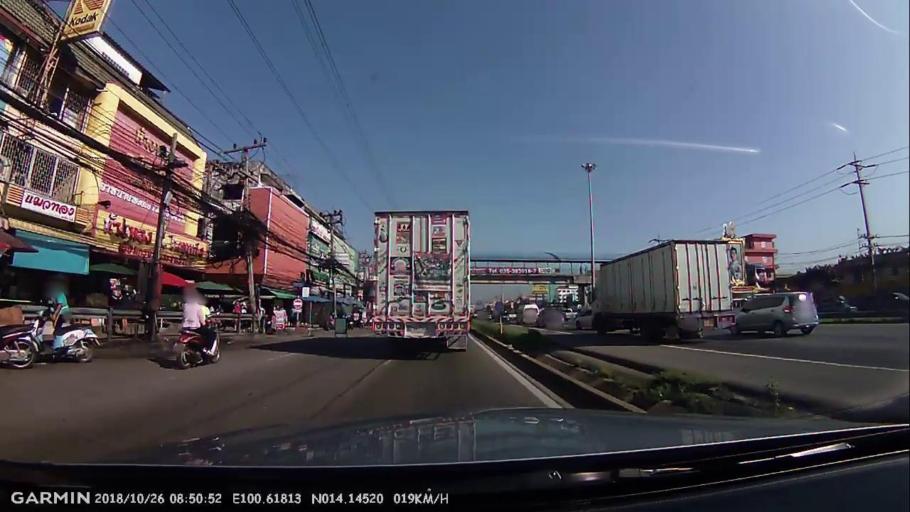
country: TH
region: Pathum Thani
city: Khlong Luang
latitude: 14.1453
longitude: 100.6181
